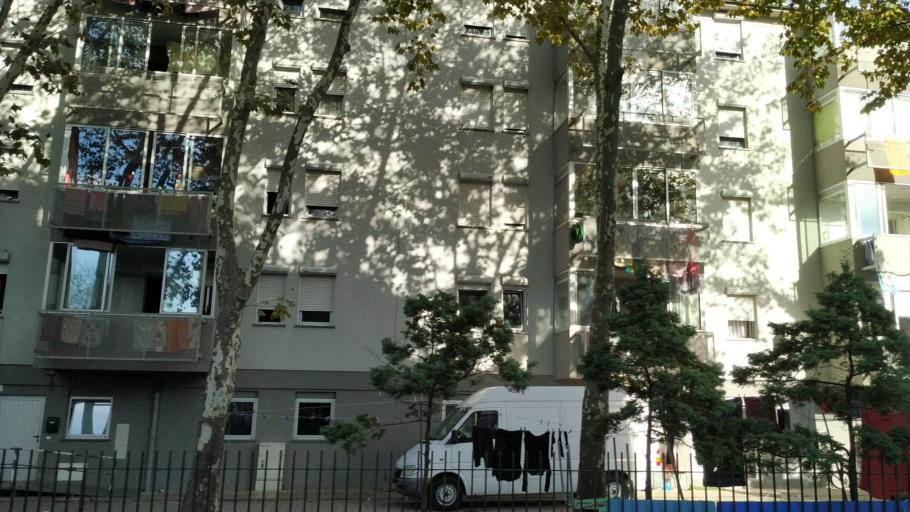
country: PT
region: Porto
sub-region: Vila Nova de Gaia
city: Vila Nova de Gaia
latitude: 41.1203
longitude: -8.6152
